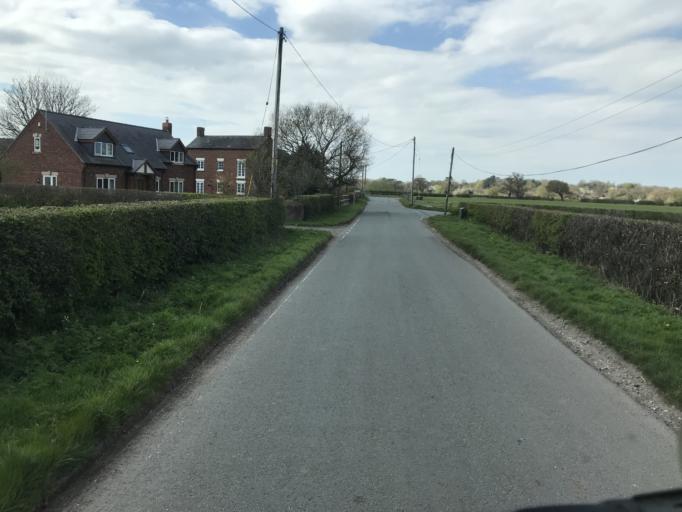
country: GB
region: England
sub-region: Cheshire West and Chester
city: Tarvin
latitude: 53.2115
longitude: -2.7725
